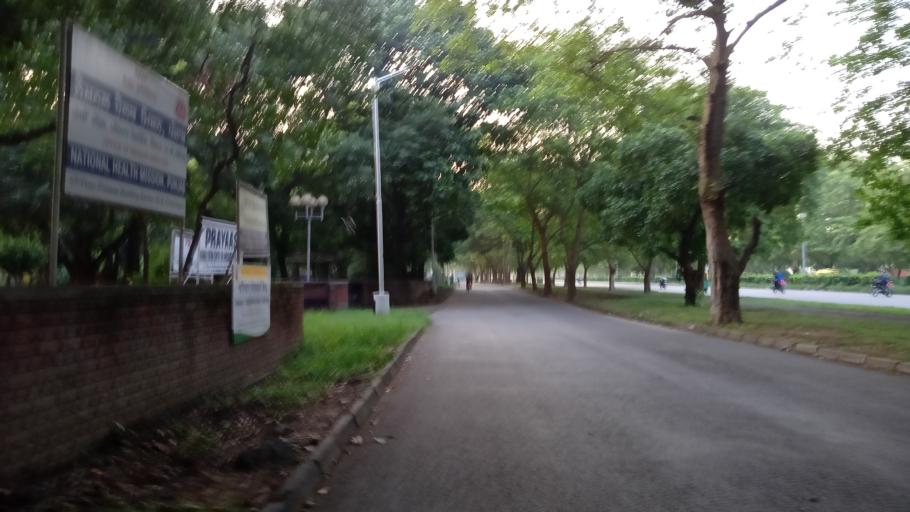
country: IN
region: Chandigarh
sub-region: Chandigarh
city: Chandigarh
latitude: 30.7465
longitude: 76.7524
